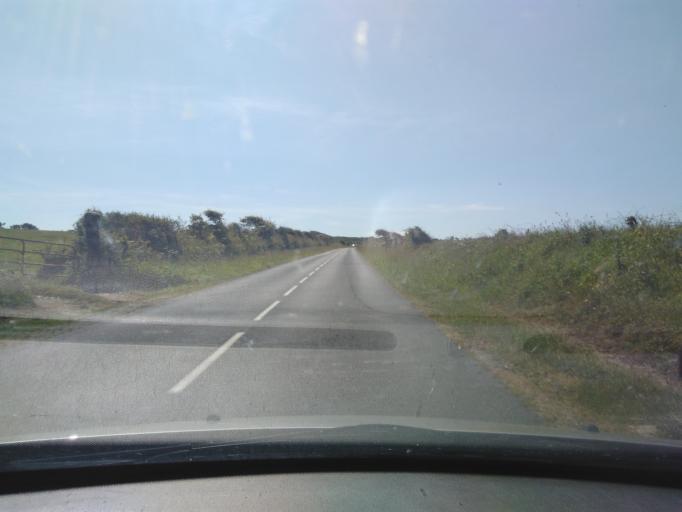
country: FR
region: Lower Normandy
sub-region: Departement de la Manche
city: Beaumont-Hague
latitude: 49.7023
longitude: -1.9292
